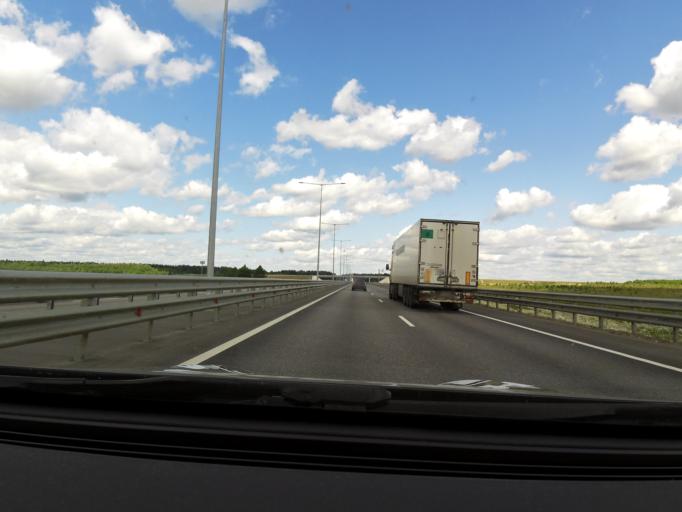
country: RU
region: Tverskaya
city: Vydropuzhsk
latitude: 57.2505
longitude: 34.8865
